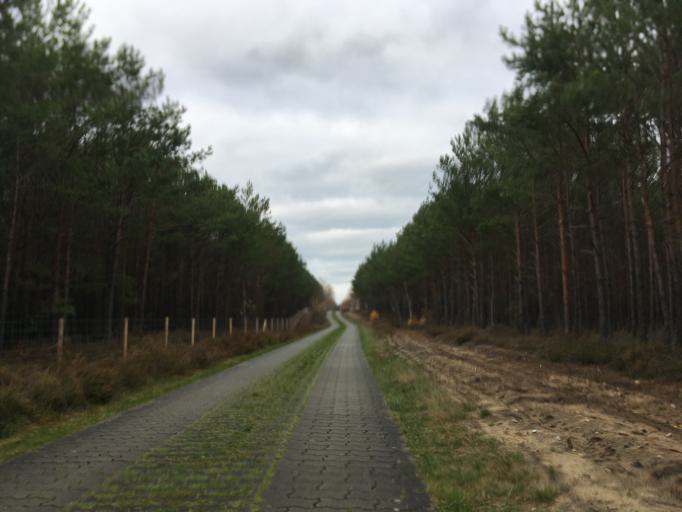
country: DE
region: Brandenburg
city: Tauer
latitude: 52.0010
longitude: 14.5065
